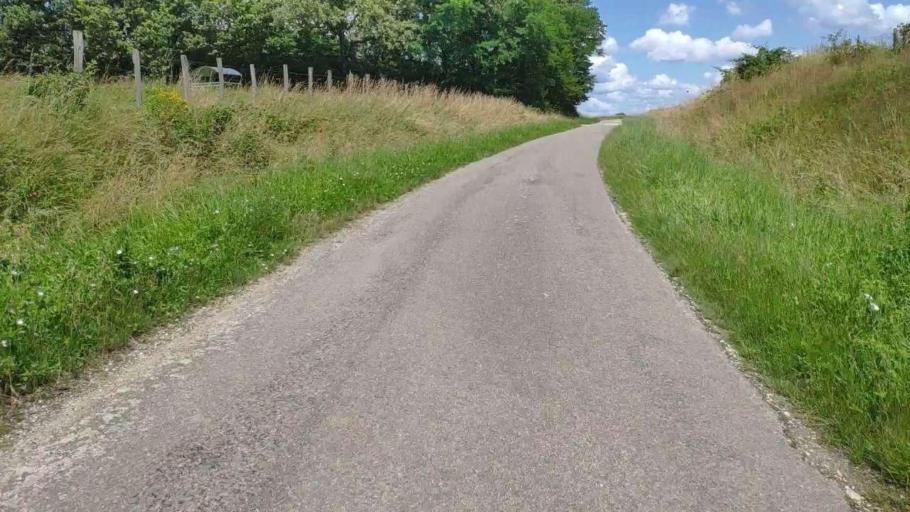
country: FR
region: Franche-Comte
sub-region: Departement du Jura
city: Chaussin
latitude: 46.8756
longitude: 5.4755
